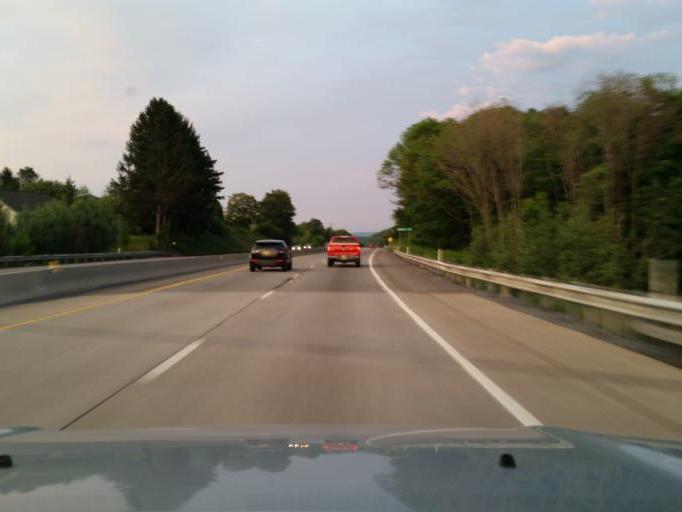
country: US
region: Pennsylvania
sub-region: Cambria County
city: Ebensburg
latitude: 40.4747
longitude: -78.7434
